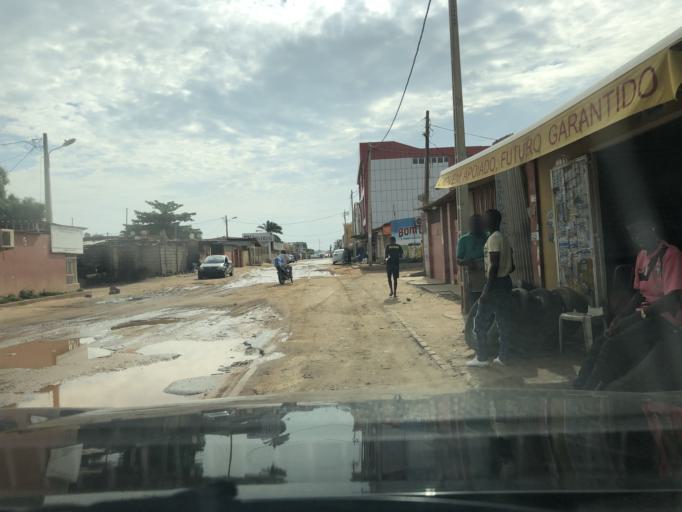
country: AO
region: Luanda
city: Luanda
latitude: -8.8420
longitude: 13.2612
